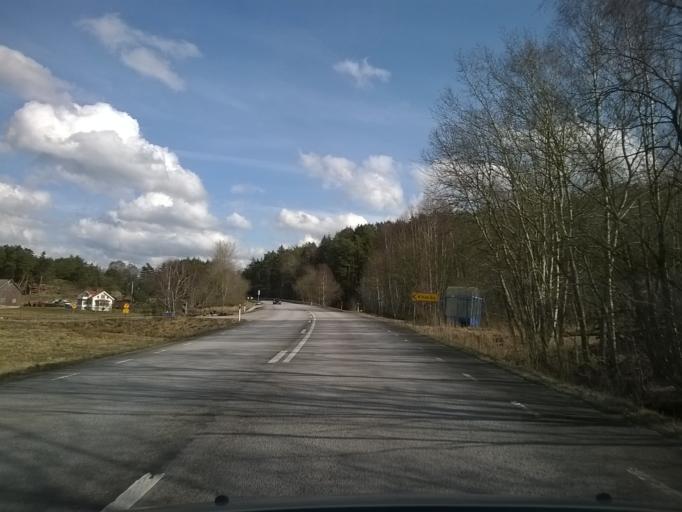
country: SE
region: Vaestra Goetaland
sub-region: Tjorns Kommun
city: Myggenas
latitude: 58.0633
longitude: 11.7244
